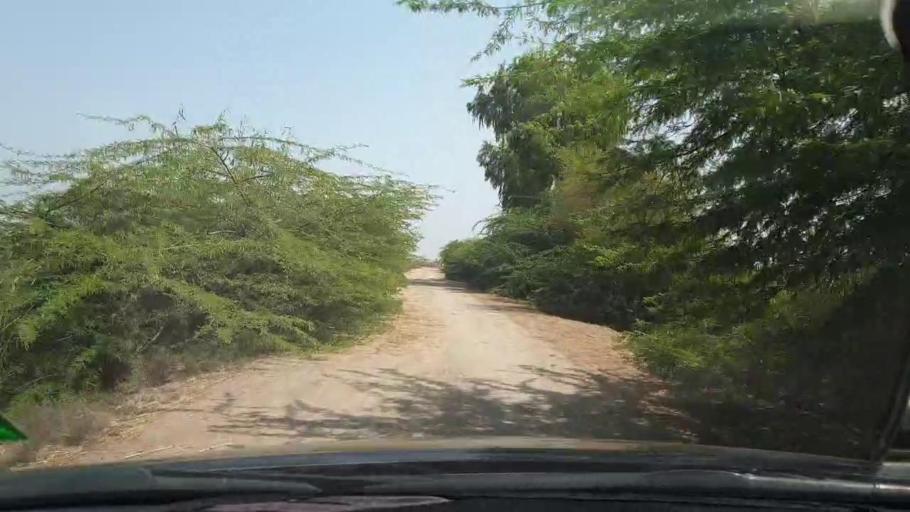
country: PK
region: Sindh
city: Tando Bago
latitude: 24.8005
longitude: 69.1051
